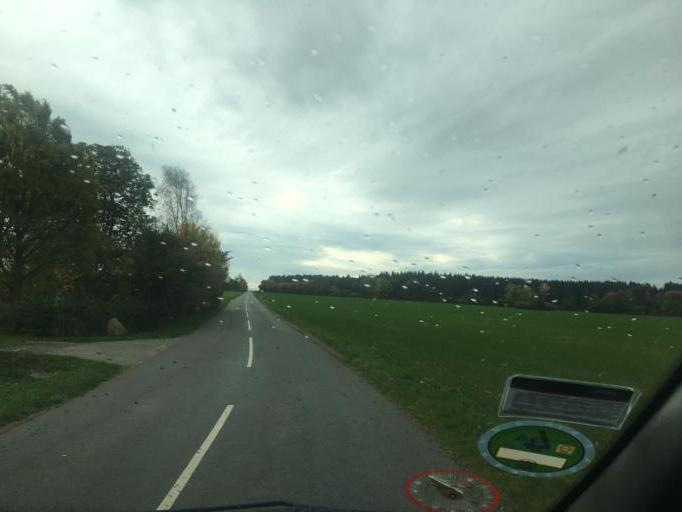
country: DK
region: Zealand
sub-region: Koge Kommune
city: Bjaeverskov
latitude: 55.4216
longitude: 11.9820
